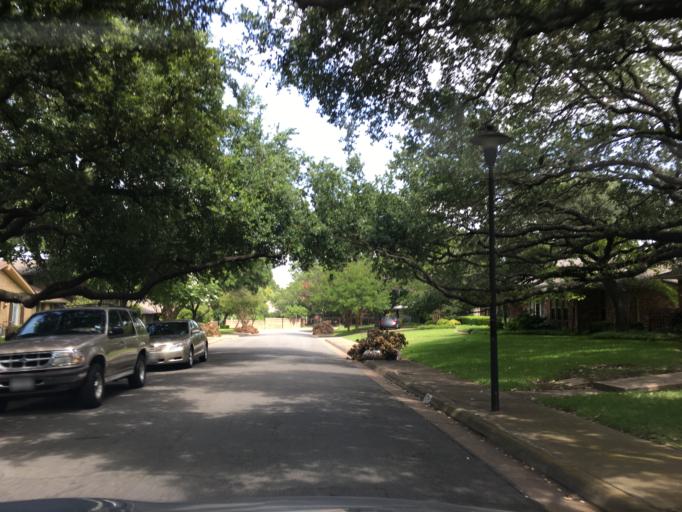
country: US
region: Texas
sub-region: Dallas County
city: University Park
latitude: 32.8795
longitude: -96.7799
